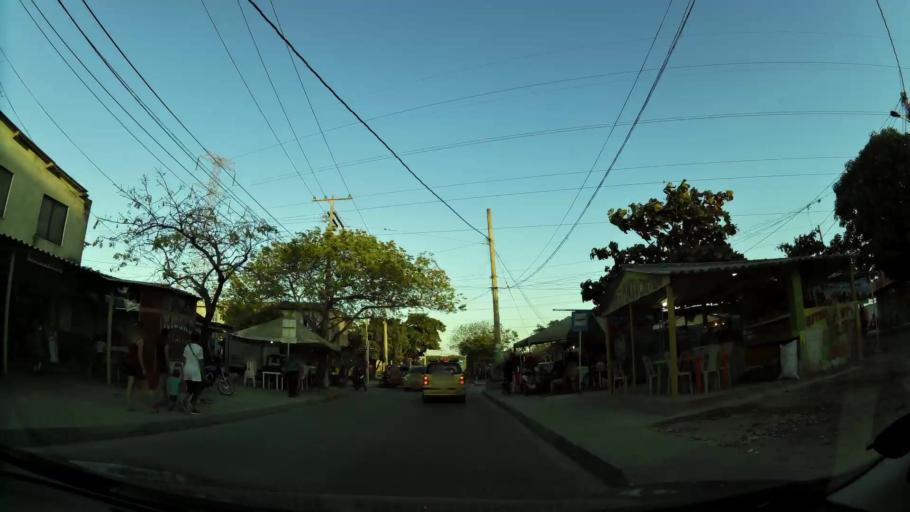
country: CO
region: Atlantico
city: Soledad
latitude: 10.9214
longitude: -74.7898
